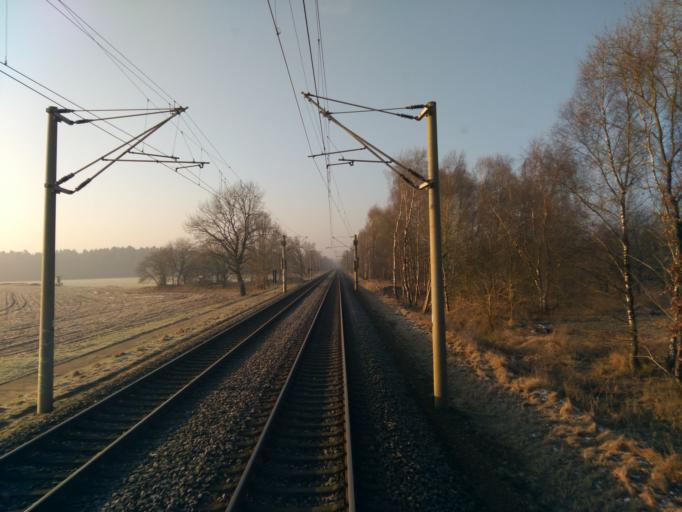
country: DE
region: Lower Saxony
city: Buchholz in der Nordheide
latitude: 53.3447
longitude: 9.9081
